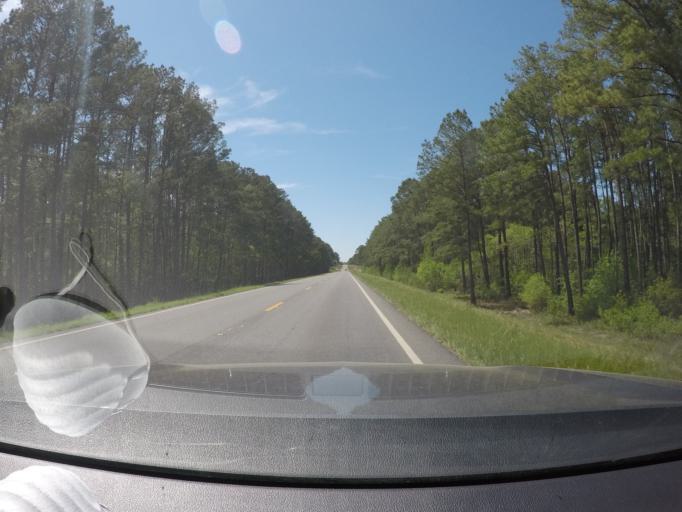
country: US
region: Georgia
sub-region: Evans County
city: Claxton
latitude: 32.1493
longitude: -81.7873
